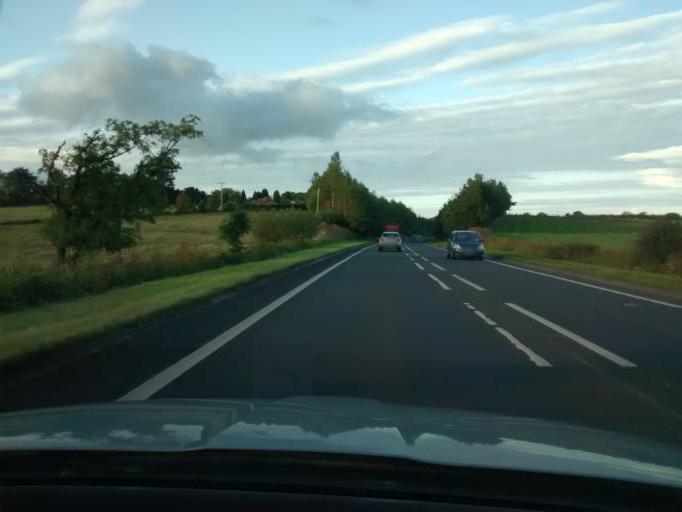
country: GB
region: Scotland
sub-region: Renfrewshire
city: Kilbarchan
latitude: 55.8243
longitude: -4.5415
